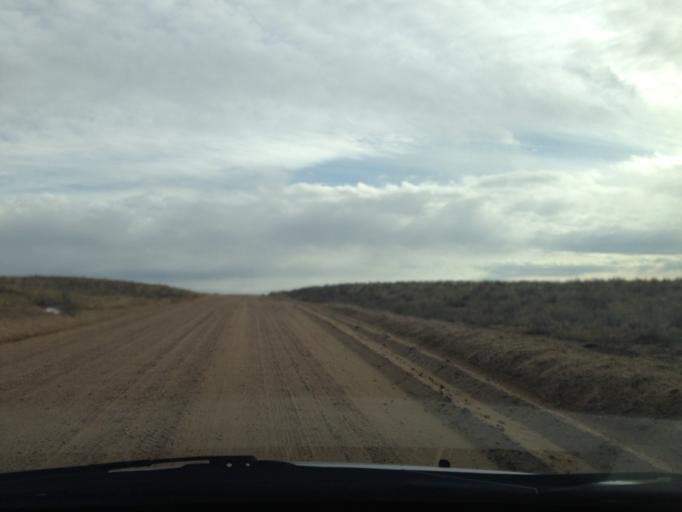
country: US
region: Colorado
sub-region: Weld County
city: Keenesburg
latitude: 40.2512
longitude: -104.2068
